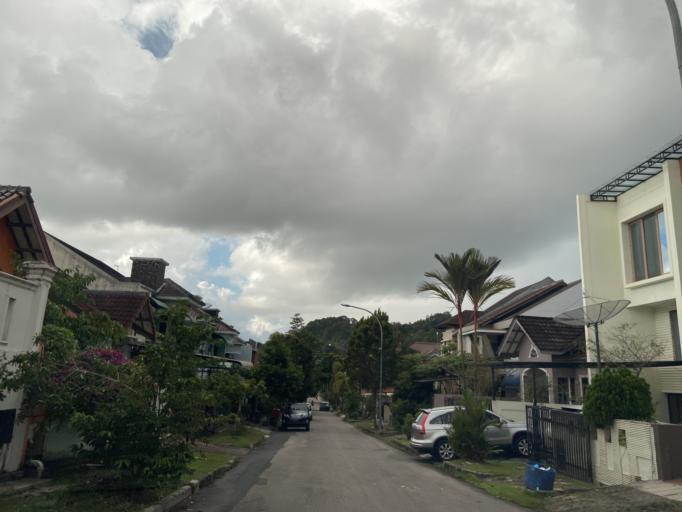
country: SG
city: Singapore
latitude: 1.1051
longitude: 104.0243
